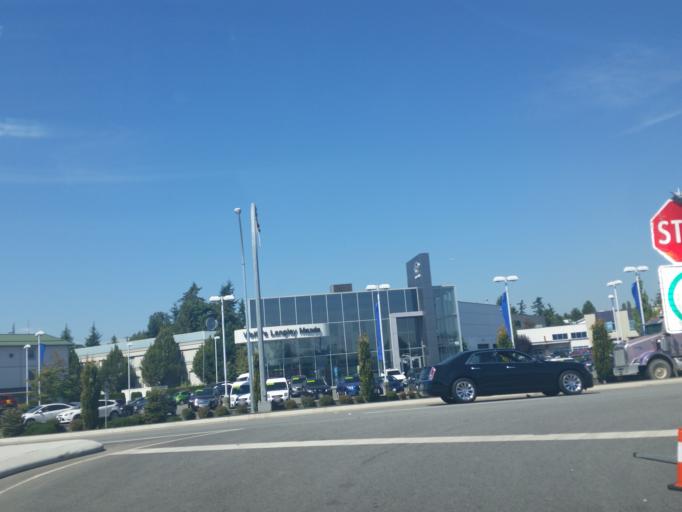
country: CA
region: British Columbia
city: Langley
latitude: 49.1048
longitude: -122.6888
